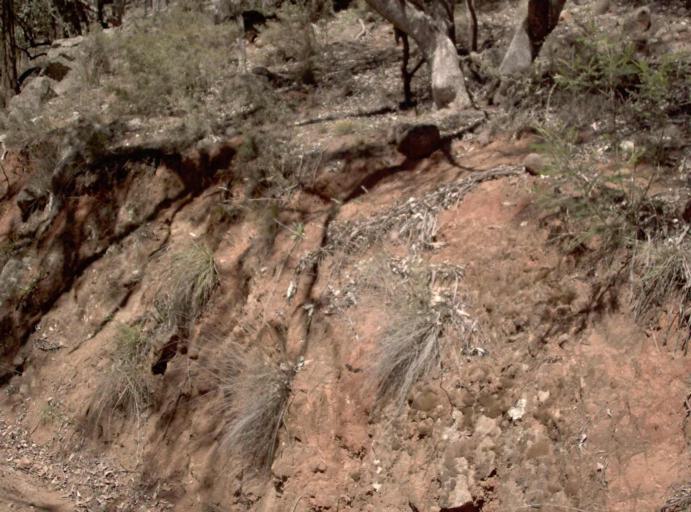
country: AU
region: New South Wales
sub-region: Snowy River
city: Jindabyne
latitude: -37.0581
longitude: 148.5300
